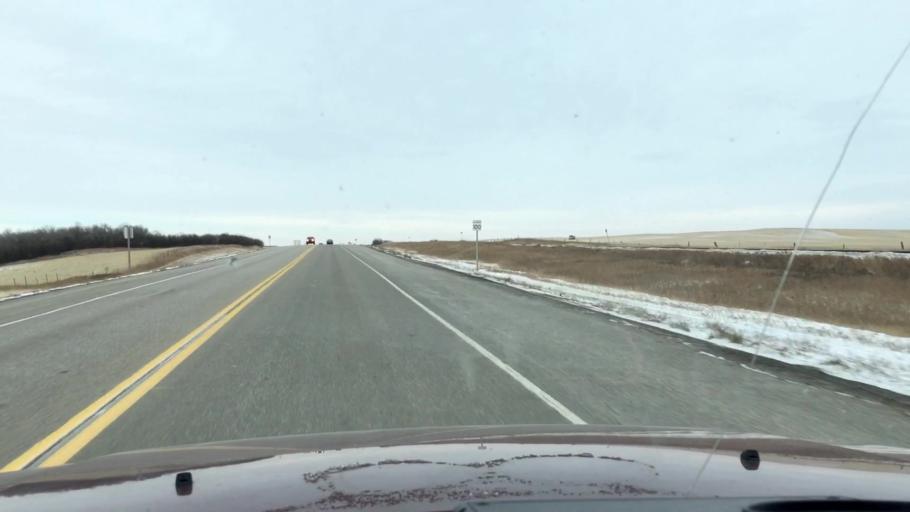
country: CA
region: Saskatchewan
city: Moose Jaw
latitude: 50.8472
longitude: -105.5599
